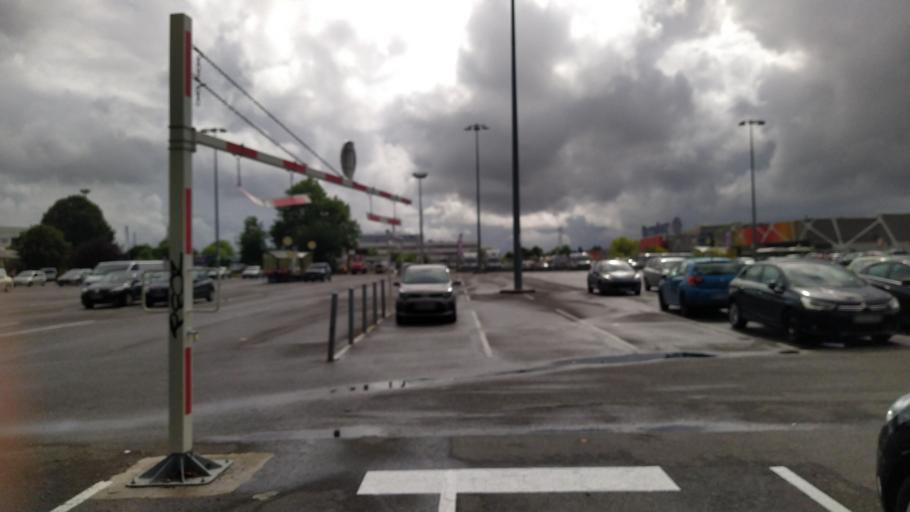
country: FR
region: Pays de la Loire
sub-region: Departement de la Loire-Atlantique
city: Sainte-Luce-sur-Loire
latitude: 47.2580
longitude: -1.5100
